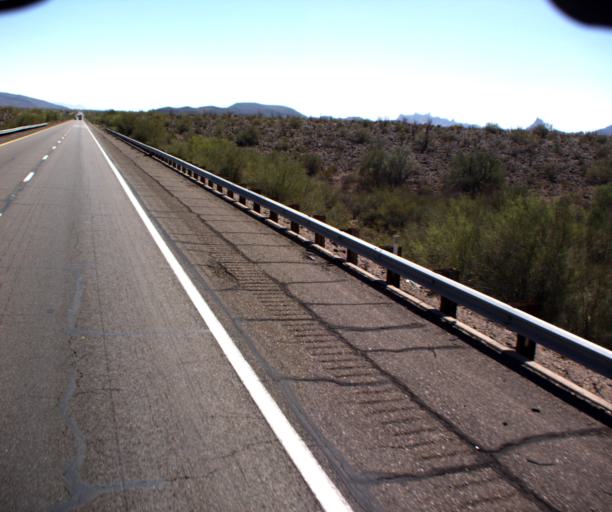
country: US
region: Arizona
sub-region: La Paz County
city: Quartzsite
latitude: 33.6600
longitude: -113.9986
